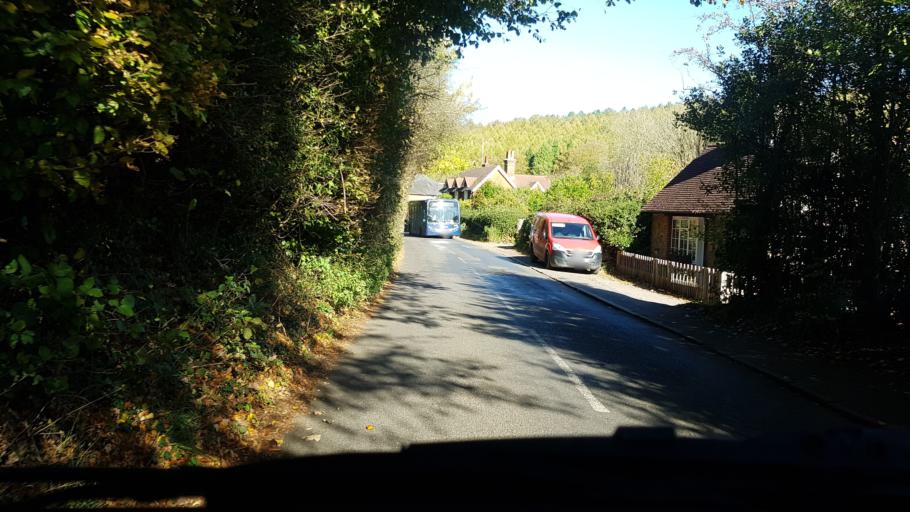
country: GB
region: England
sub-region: Surrey
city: Ockley
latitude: 51.1915
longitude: -0.4113
